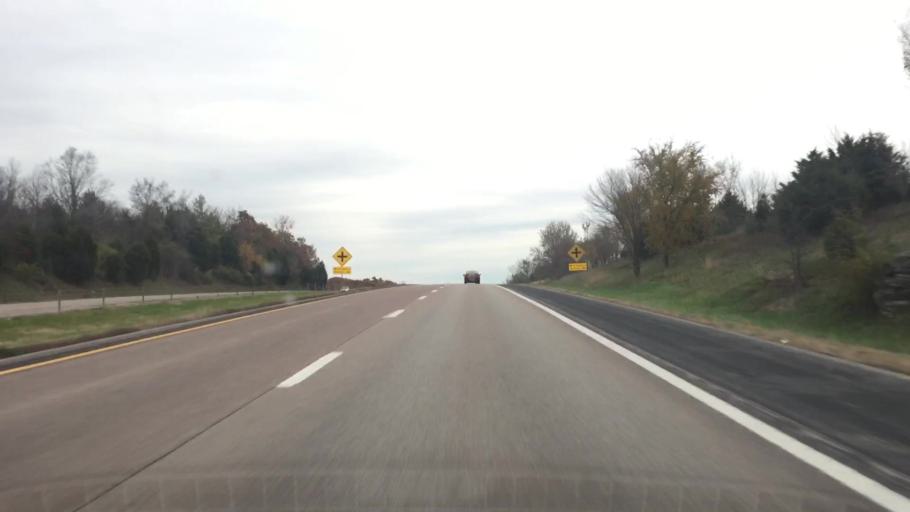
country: US
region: Missouri
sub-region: Boone County
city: Ashland
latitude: 38.6935
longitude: -92.2548
